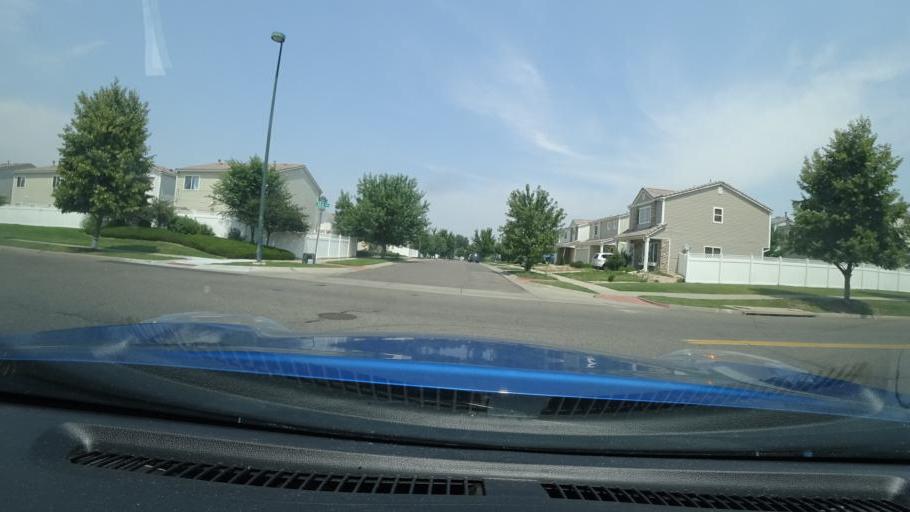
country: US
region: Colorado
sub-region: Adams County
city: Aurora
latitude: 39.7746
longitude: -104.7697
